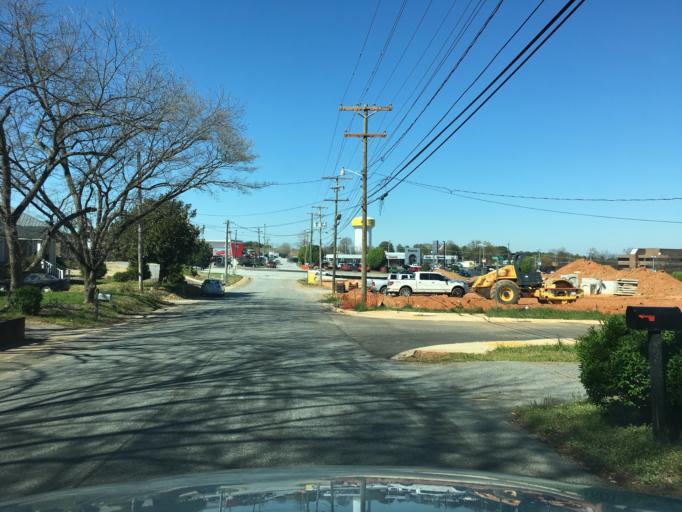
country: US
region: South Carolina
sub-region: Greenville County
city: Greer
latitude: 34.9472
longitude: -82.2378
